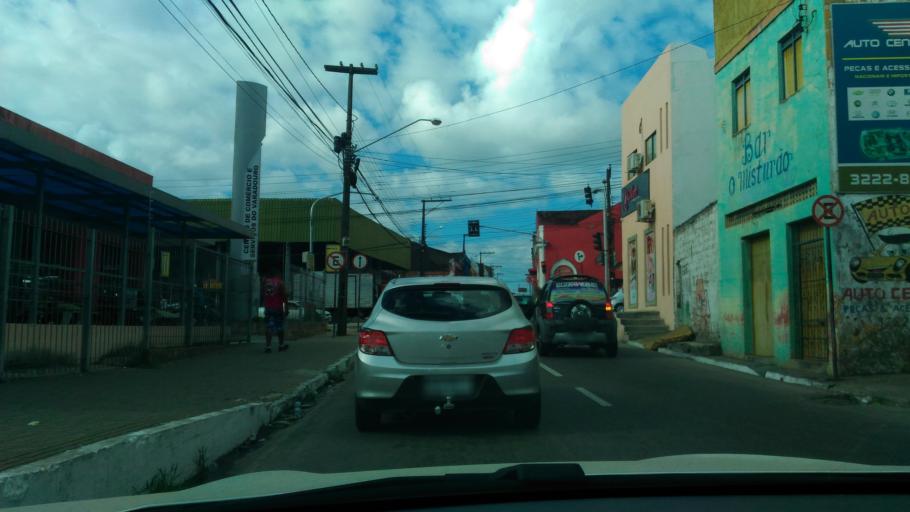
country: BR
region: Paraiba
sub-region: Joao Pessoa
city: Joao Pessoa
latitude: -7.1188
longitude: -34.8890
